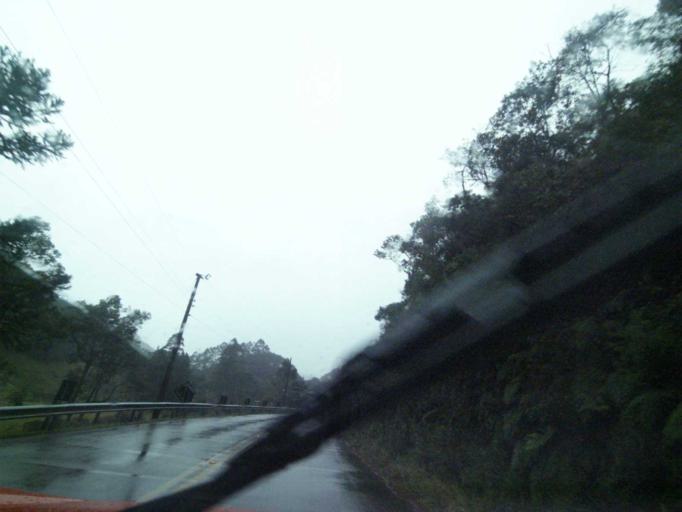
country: BR
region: Santa Catarina
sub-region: Anitapolis
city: Anitapolis
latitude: -27.7880
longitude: -49.0432
